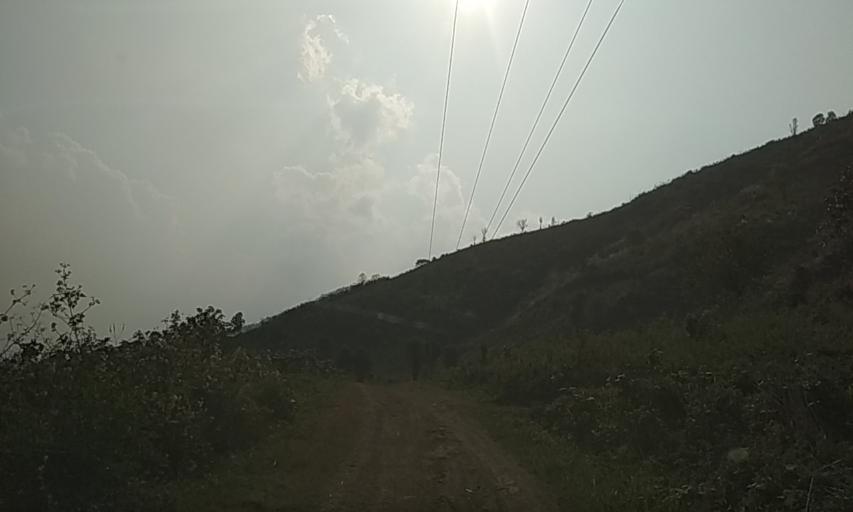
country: LA
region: Louangphabang
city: Louangphabang
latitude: 20.0348
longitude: 101.7932
